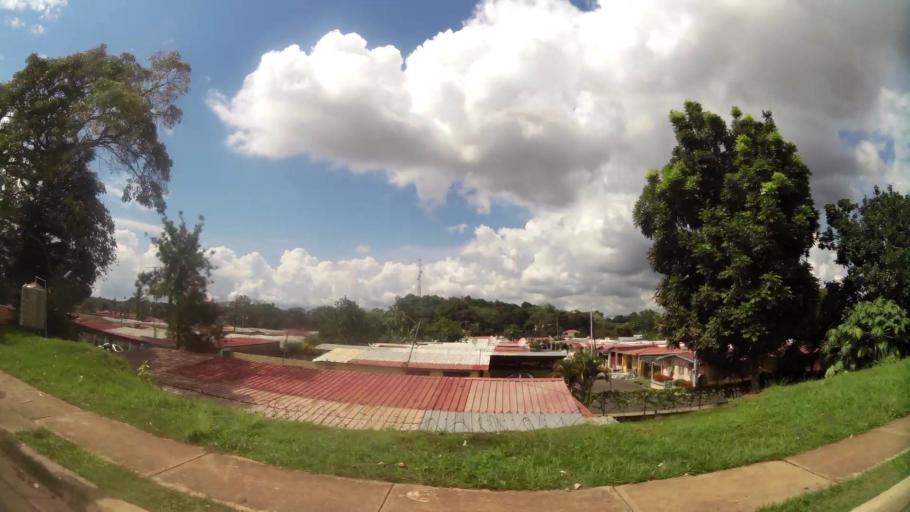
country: PA
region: Panama
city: Nuevo Arraijan
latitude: 8.9214
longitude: -79.7075
